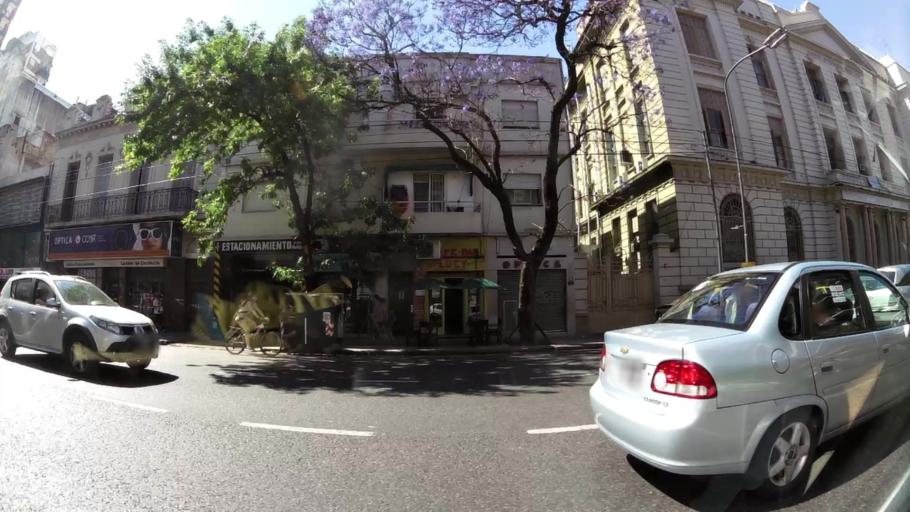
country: AR
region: Buenos Aires F.D.
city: Buenos Aires
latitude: -34.6228
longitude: -58.3947
